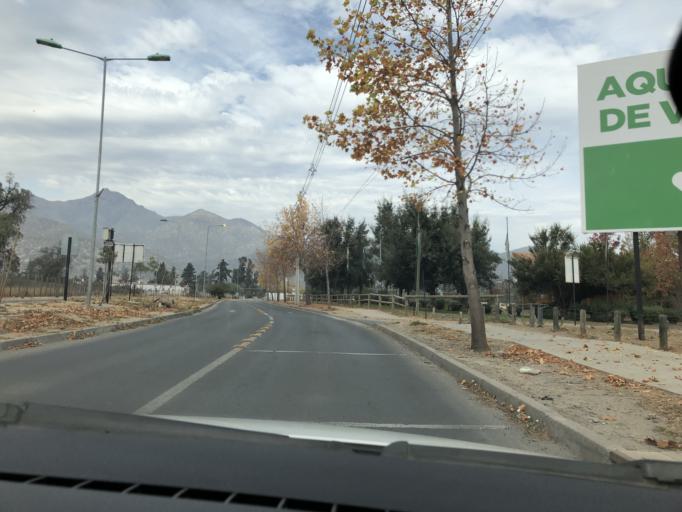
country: CL
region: Santiago Metropolitan
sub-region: Provincia de Cordillera
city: Puente Alto
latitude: -33.5951
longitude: -70.5107
